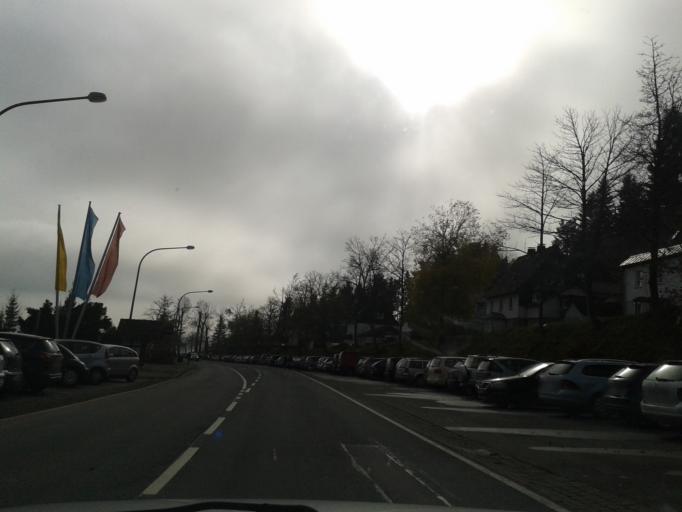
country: DE
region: North Rhine-Westphalia
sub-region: Regierungsbezirk Arnsberg
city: Winterberg
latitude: 51.1678
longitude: 8.4857
